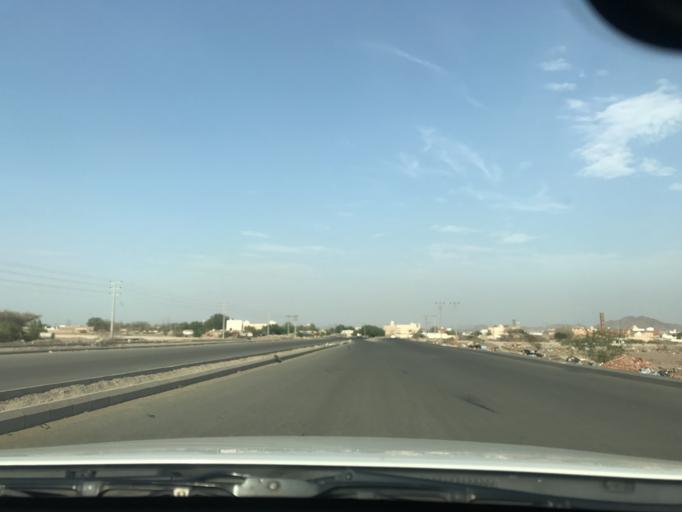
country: SA
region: Makkah
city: Al Jumum
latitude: 21.4541
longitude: 39.5446
